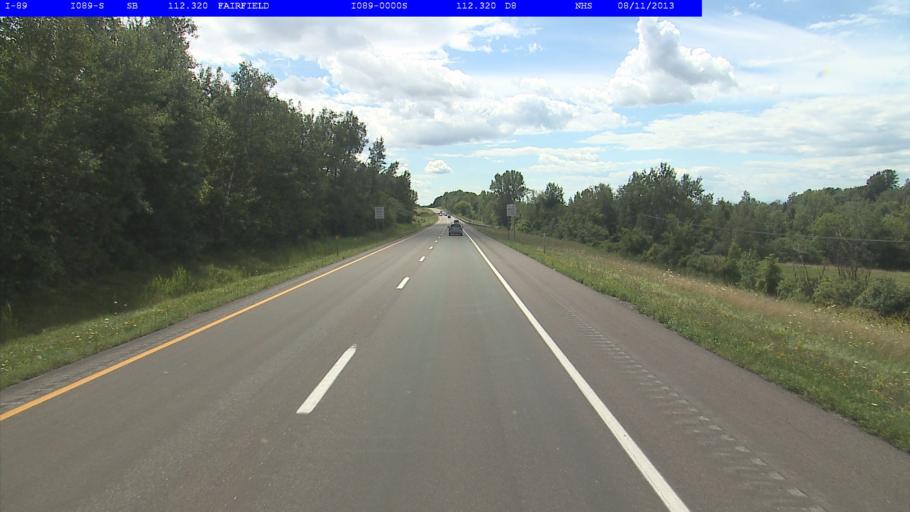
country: US
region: Vermont
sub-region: Franklin County
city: Saint Albans
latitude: 44.7746
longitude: -73.0751
